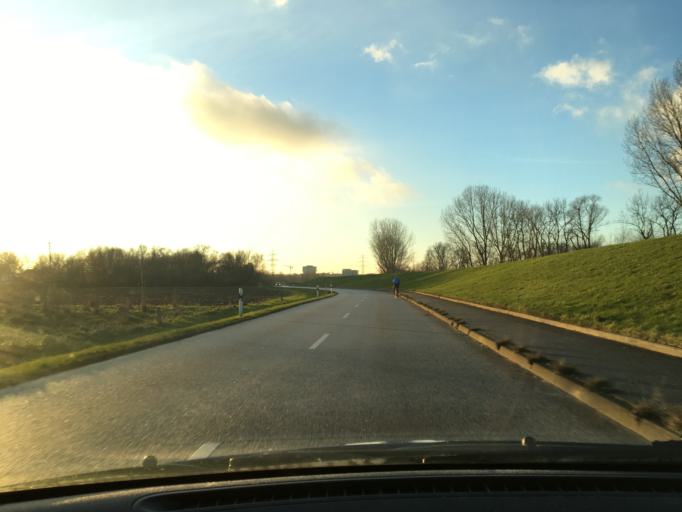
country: DE
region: Hamburg
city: Harburg
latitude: 53.4697
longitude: 10.0131
